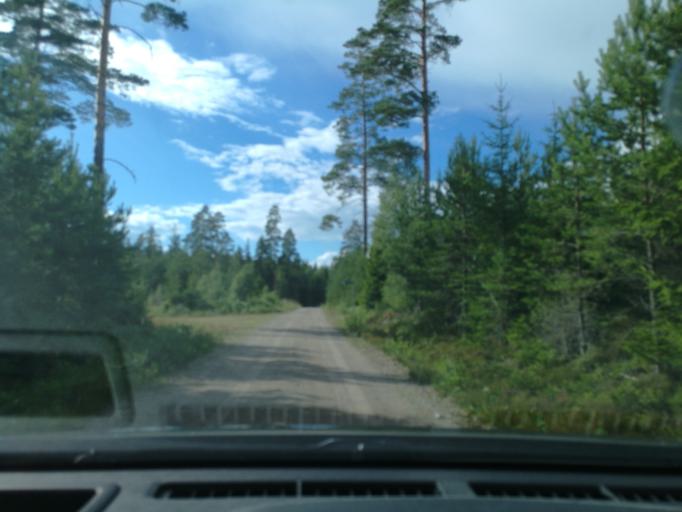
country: SE
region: Vaestmanland
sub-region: Surahammars Kommun
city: Ramnas
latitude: 59.8318
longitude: 16.2441
